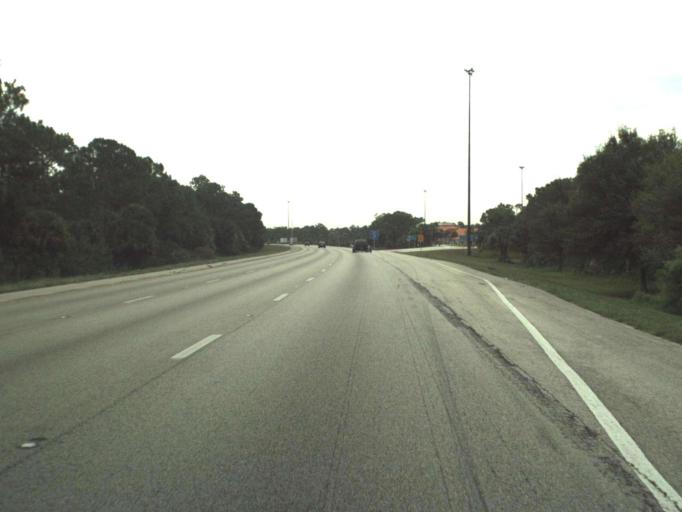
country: US
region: Florida
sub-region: Martin County
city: Palm City
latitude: 27.1282
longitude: -80.3461
